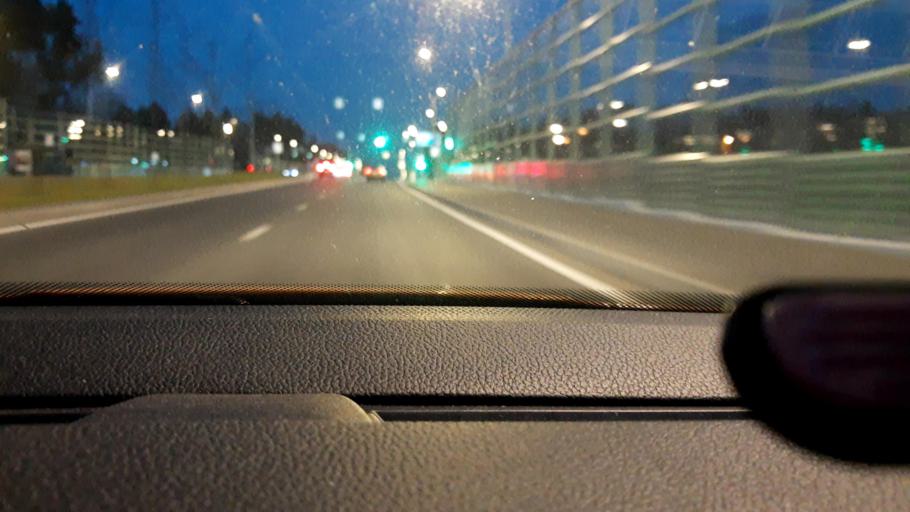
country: RU
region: Moskovskaya
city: Filimonki
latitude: 55.5702
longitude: 37.3566
